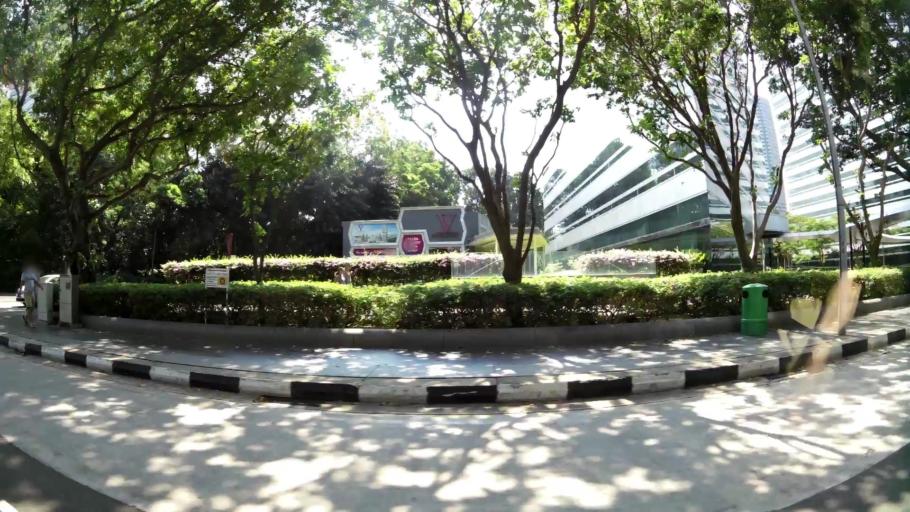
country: SG
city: Singapore
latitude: 1.2994
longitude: 103.8591
